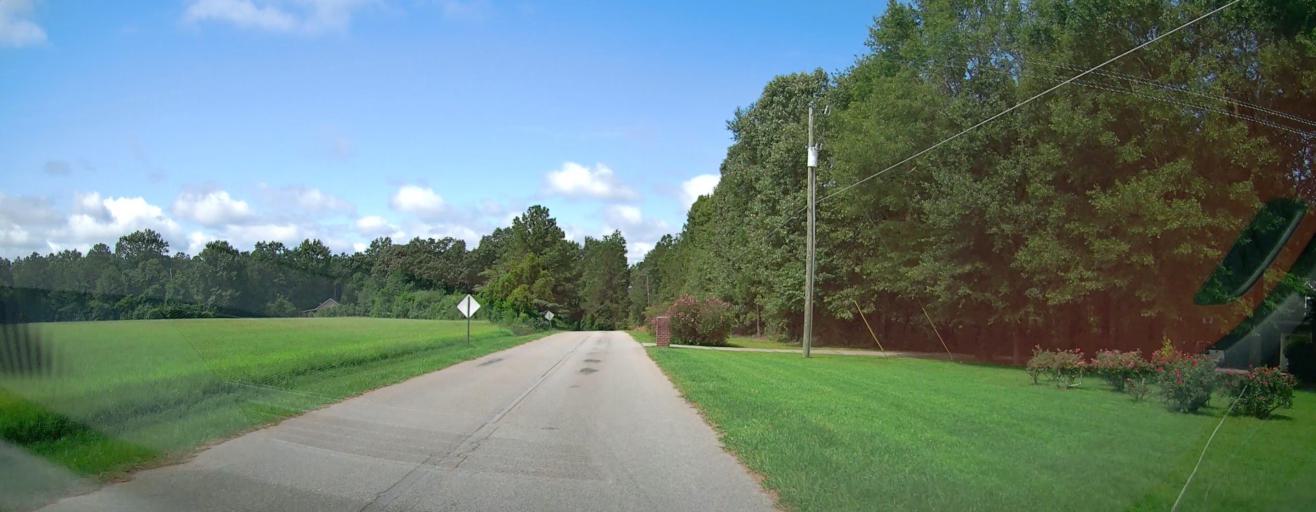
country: US
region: Georgia
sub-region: Peach County
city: Byron
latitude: 32.6625
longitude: -83.7787
